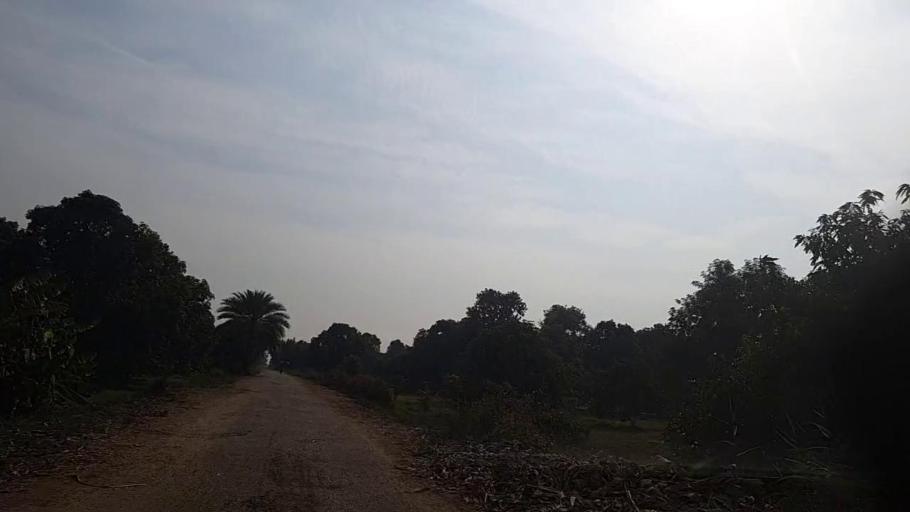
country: PK
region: Sindh
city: Daur
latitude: 26.4030
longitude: 68.2134
